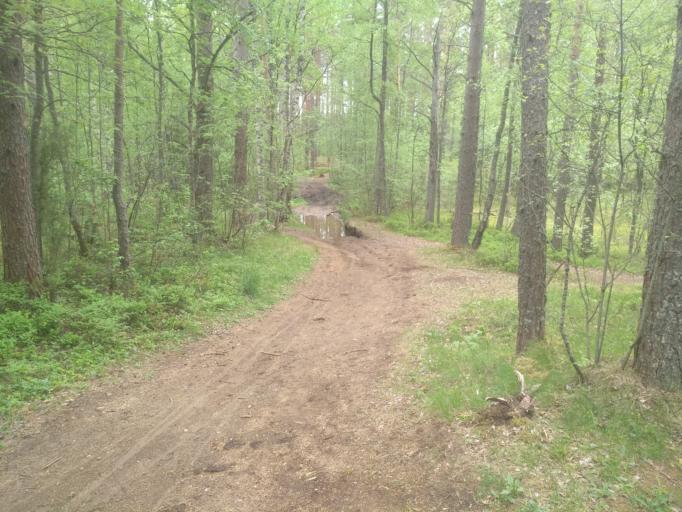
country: RU
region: Leningrad
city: Michurinskoye
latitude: 60.5896
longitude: 29.8884
